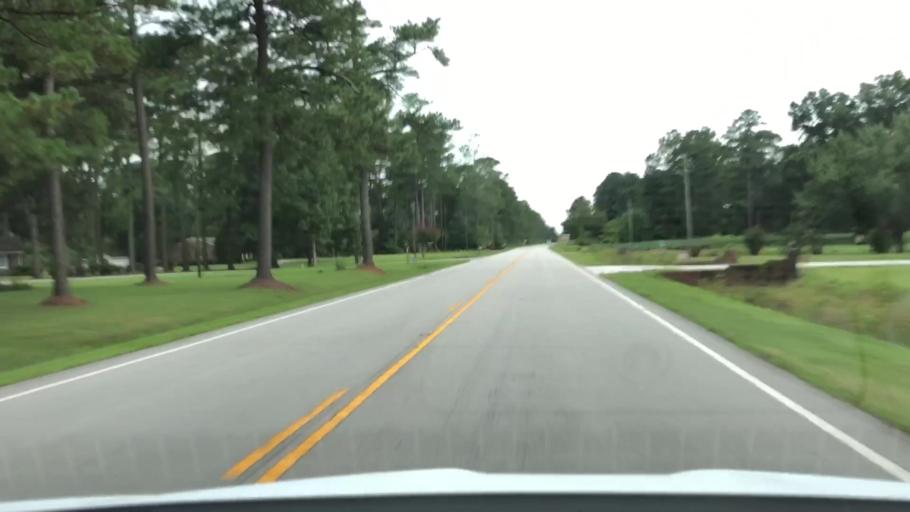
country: US
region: North Carolina
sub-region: Jones County
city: Trenton
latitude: 35.0729
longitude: -77.3820
